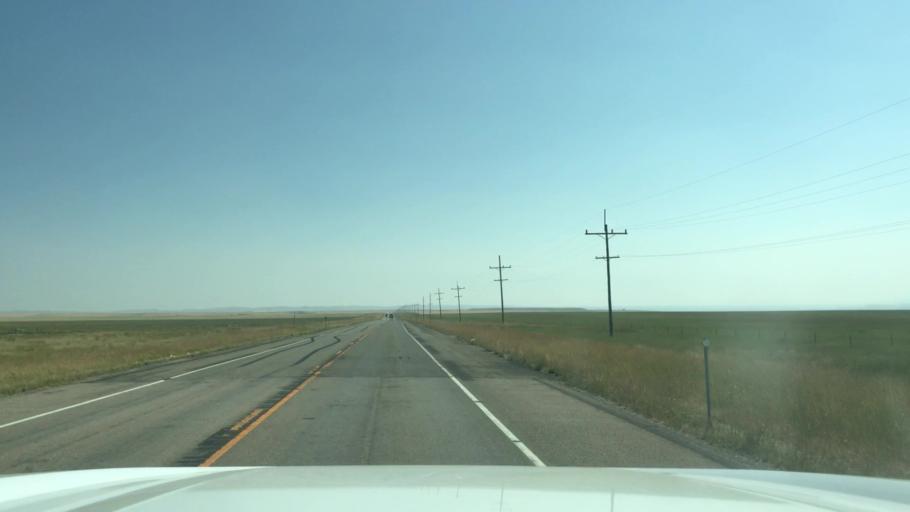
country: US
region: Montana
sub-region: Wheatland County
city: Harlowton
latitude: 46.5205
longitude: -109.7659
